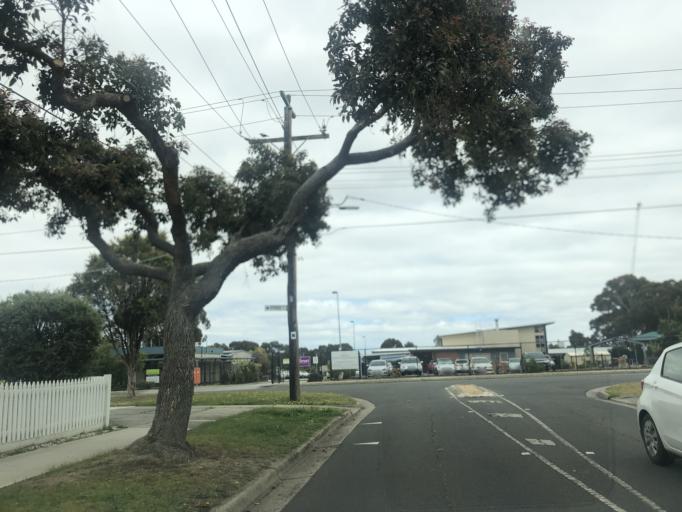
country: AU
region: Victoria
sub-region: Monash
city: Notting Hill
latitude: -37.9071
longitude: 145.1675
